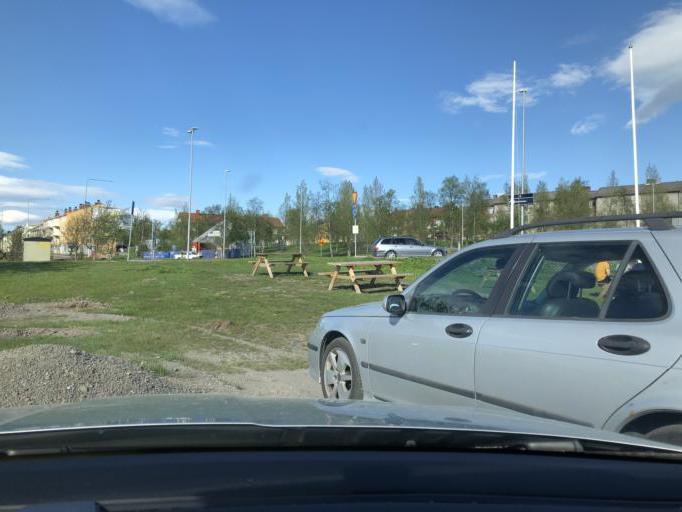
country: SE
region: Norrbotten
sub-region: Kiruna Kommun
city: Kiruna
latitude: 67.8591
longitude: 20.2227
